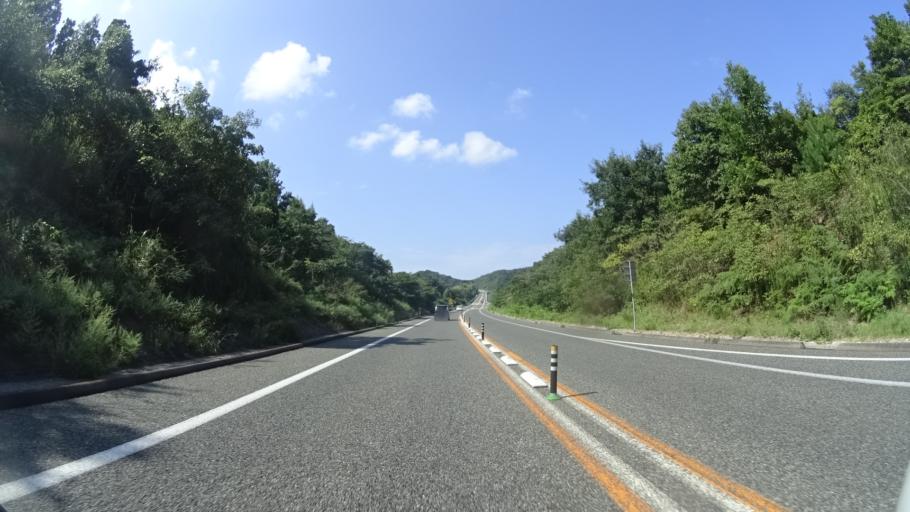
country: JP
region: Shimane
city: Hamada
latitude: 34.9202
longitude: 132.1375
